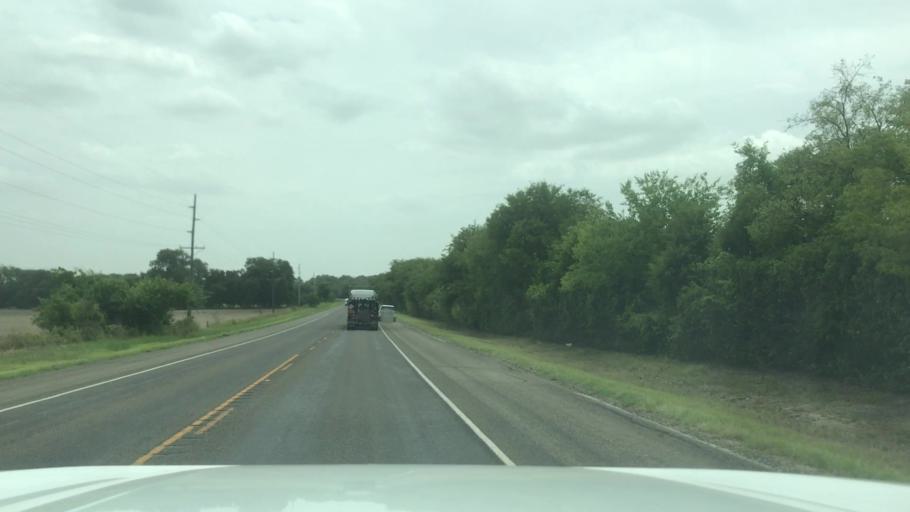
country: US
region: Texas
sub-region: Bosque County
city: Valley Mills
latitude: 31.6830
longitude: -97.5274
